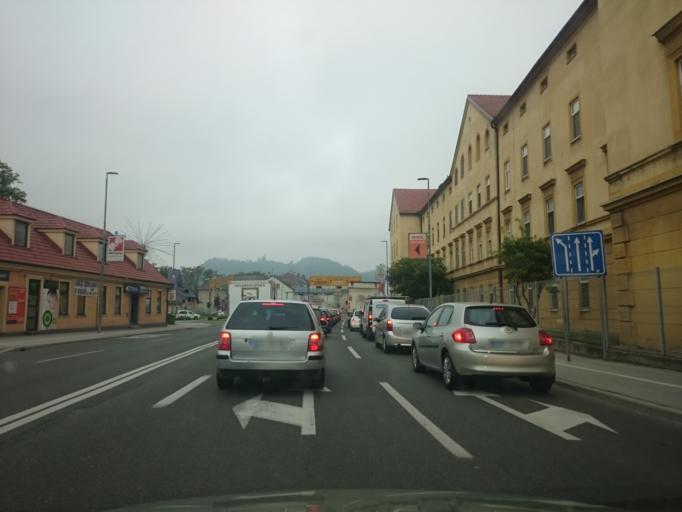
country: SI
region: Celje
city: Celje
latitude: 46.2365
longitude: 15.2720
